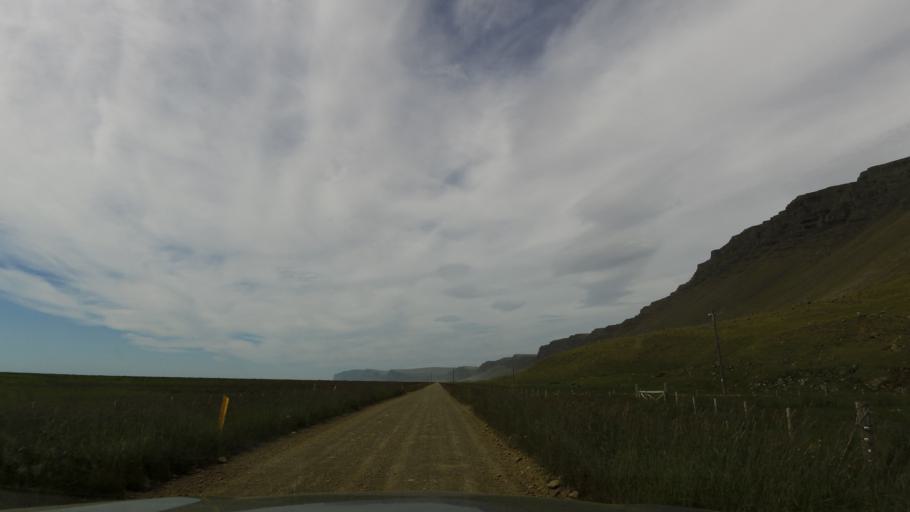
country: IS
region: West
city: Olafsvik
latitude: 65.4810
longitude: -24.0203
